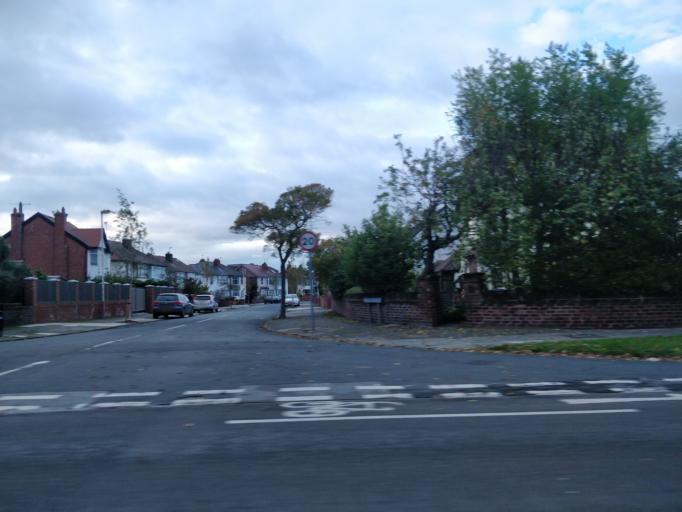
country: GB
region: England
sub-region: Sefton
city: Southport
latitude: 53.6635
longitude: -2.9641
